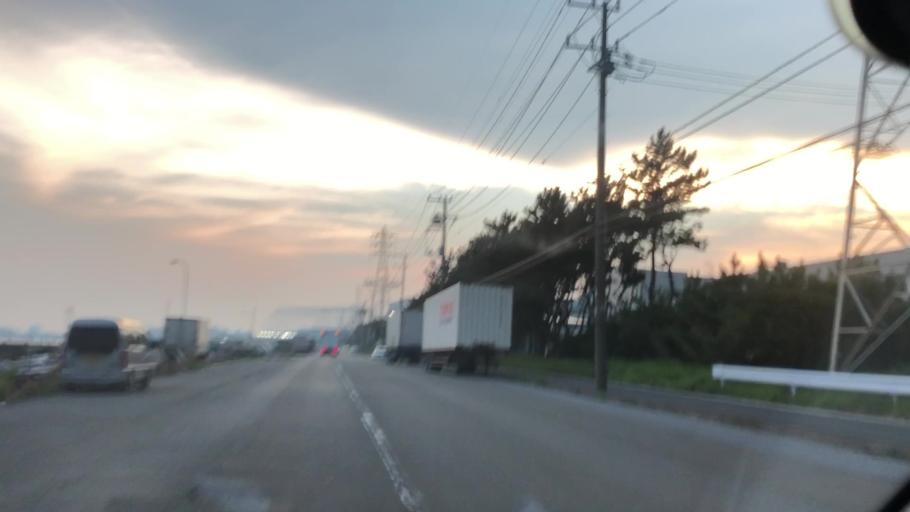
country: JP
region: Tokyo
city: Urayasu
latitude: 35.6676
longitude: 139.9389
